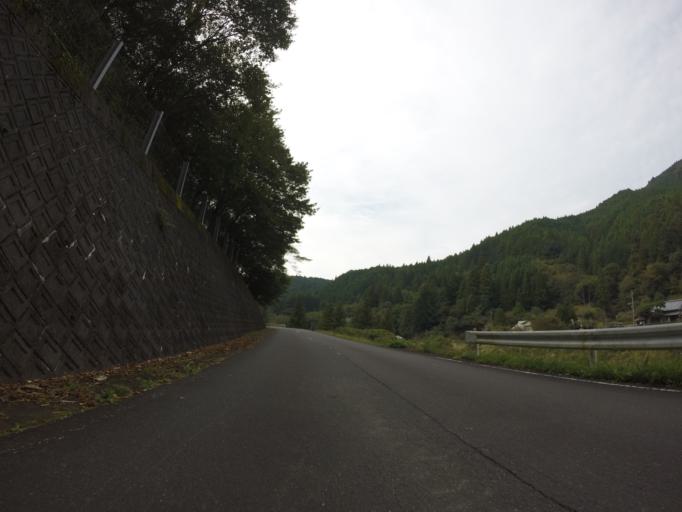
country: JP
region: Shizuoka
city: Kanaya
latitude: 34.8886
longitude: 138.0366
